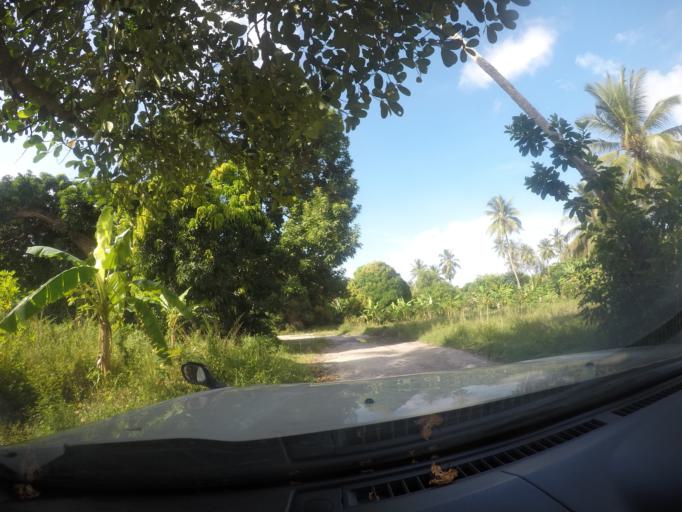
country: TZ
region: Pemba South
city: Chake Chake
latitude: -5.2486
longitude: 39.7836
